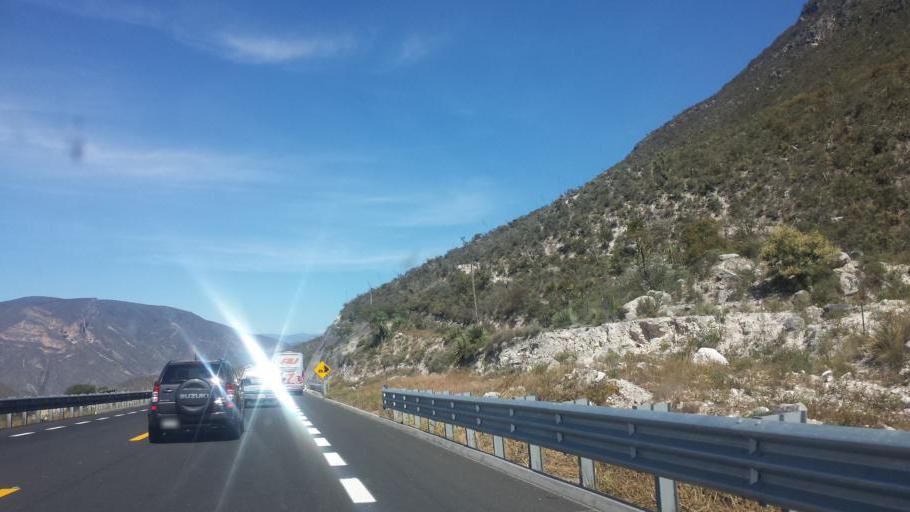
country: MX
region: Puebla
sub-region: San Jose Miahuatlan
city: San Pedro Tetitlan
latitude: 18.0770
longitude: -97.3522
